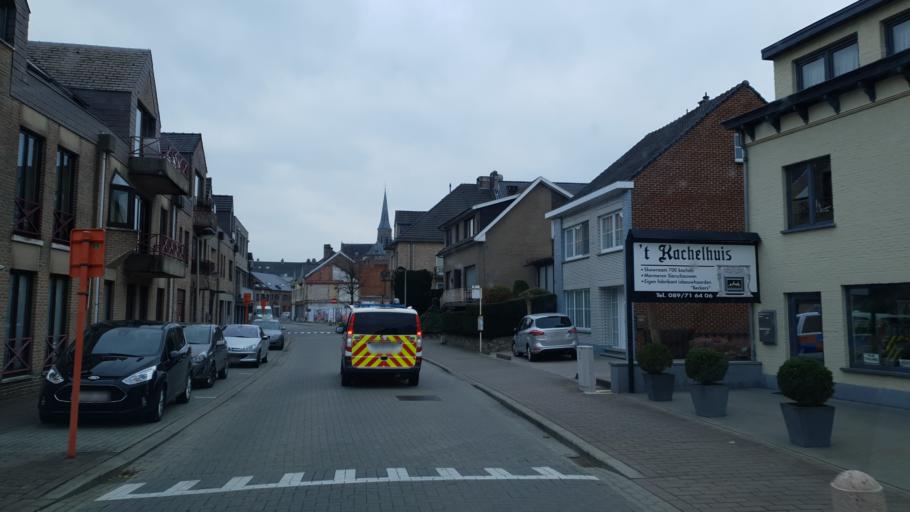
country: BE
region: Flanders
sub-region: Provincie Limburg
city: Lanaken
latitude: 50.8917
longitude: 5.6482
